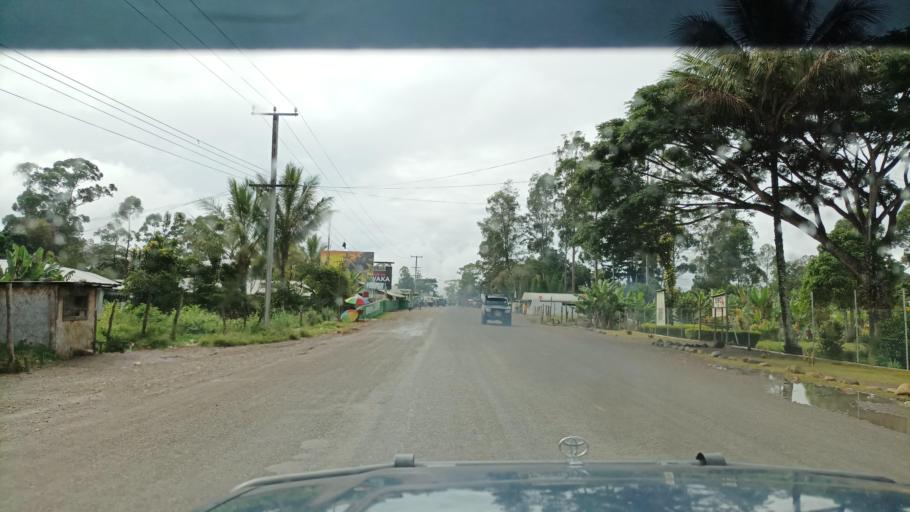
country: PG
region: Jiwaka
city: Minj
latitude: -5.8802
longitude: 144.6782
